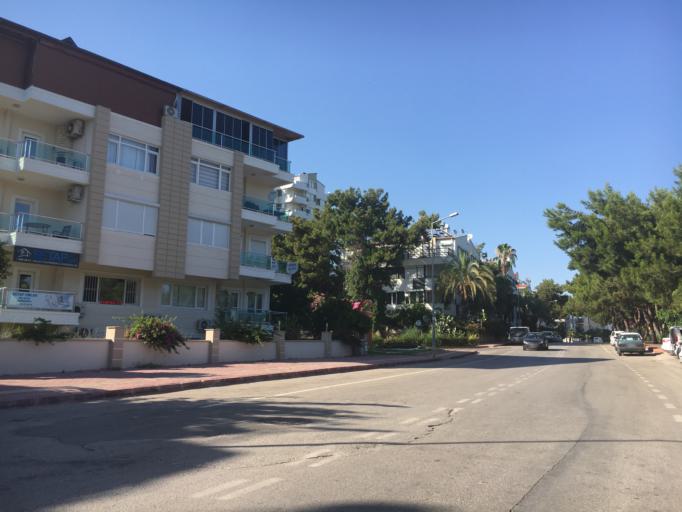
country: TR
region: Antalya
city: Antalya
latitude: 36.8639
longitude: 30.6381
